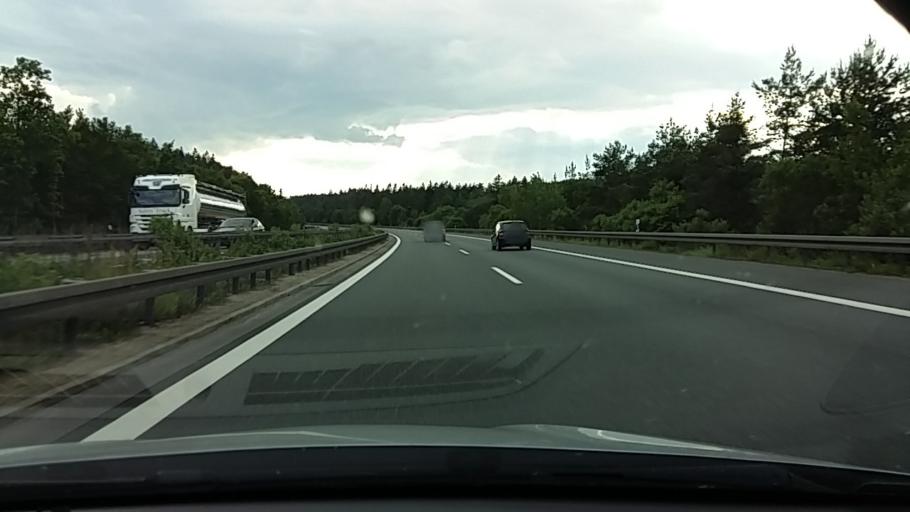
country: DE
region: Bavaria
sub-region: Upper Palatinate
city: Amberg
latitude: 49.4020
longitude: 11.8233
